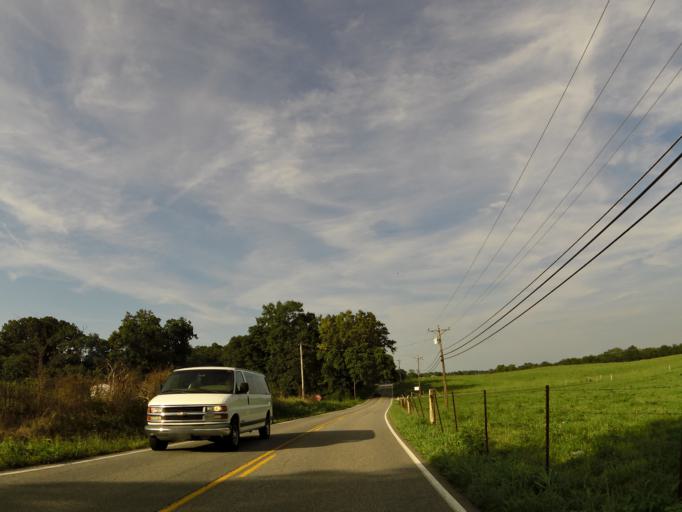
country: US
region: Tennessee
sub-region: Blount County
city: Wildwood
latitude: 35.7996
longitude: -83.8523
